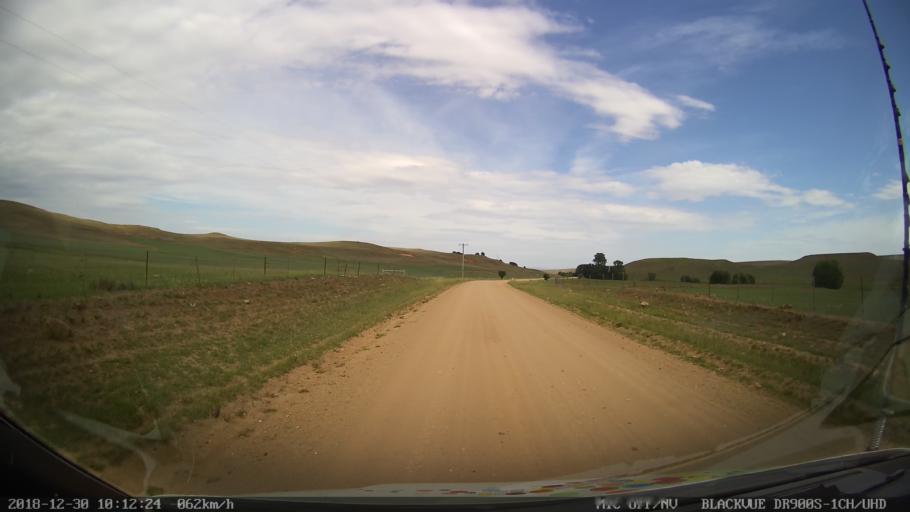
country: AU
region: New South Wales
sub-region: Snowy River
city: Berridale
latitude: -36.5420
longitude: 149.0763
